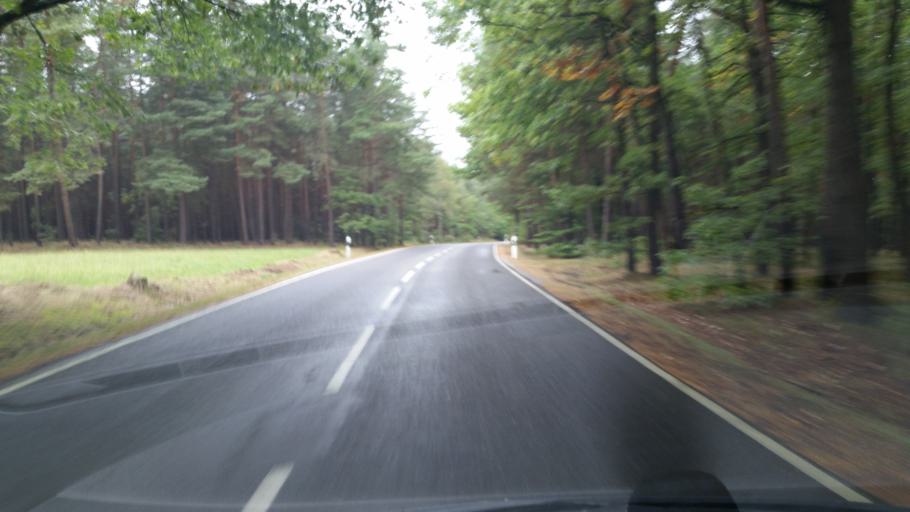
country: DE
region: Saxony
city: Neukirch
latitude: 51.3085
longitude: 14.0382
